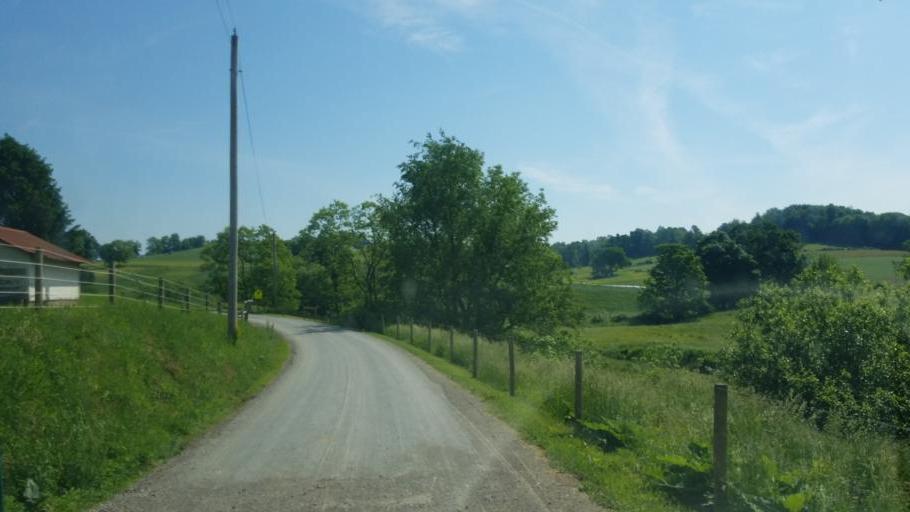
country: US
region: Ohio
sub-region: Holmes County
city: Millersburg
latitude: 40.4585
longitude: -81.7986
